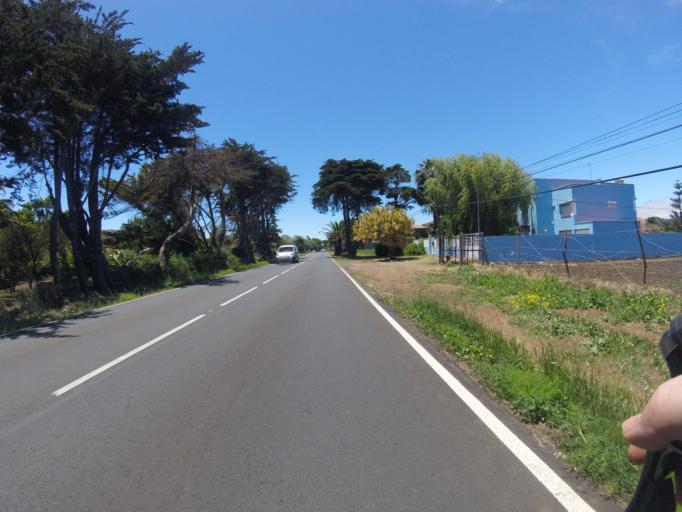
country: ES
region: Canary Islands
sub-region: Provincia de Santa Cruz de Tenerife
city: Tegueste
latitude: 28.5021
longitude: -16.3128
